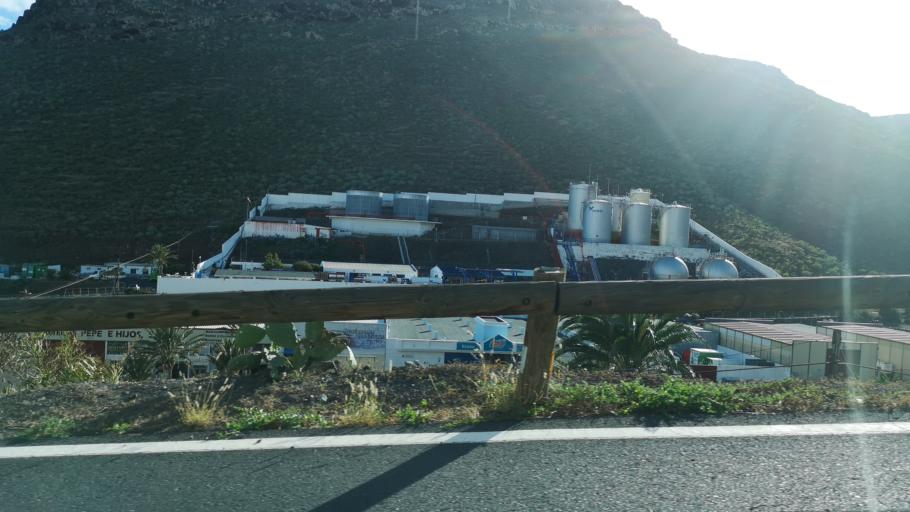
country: ES
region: Canary Islands
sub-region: Provincia de Santa Cruz de Tenerife
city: San Sebastian de la Gomera
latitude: 28.0896
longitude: -17.1172
